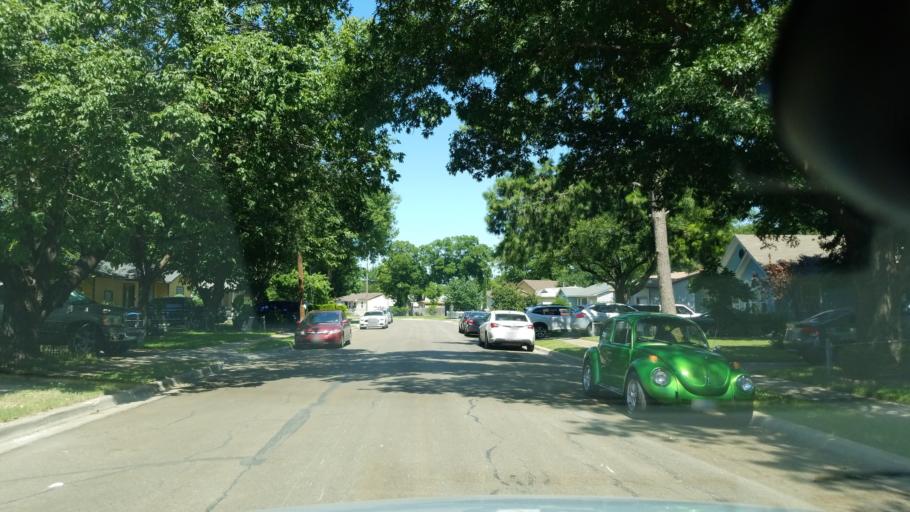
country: US
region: Texas
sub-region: Dallas County
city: Irving
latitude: 32.8306
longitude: -96.9347
